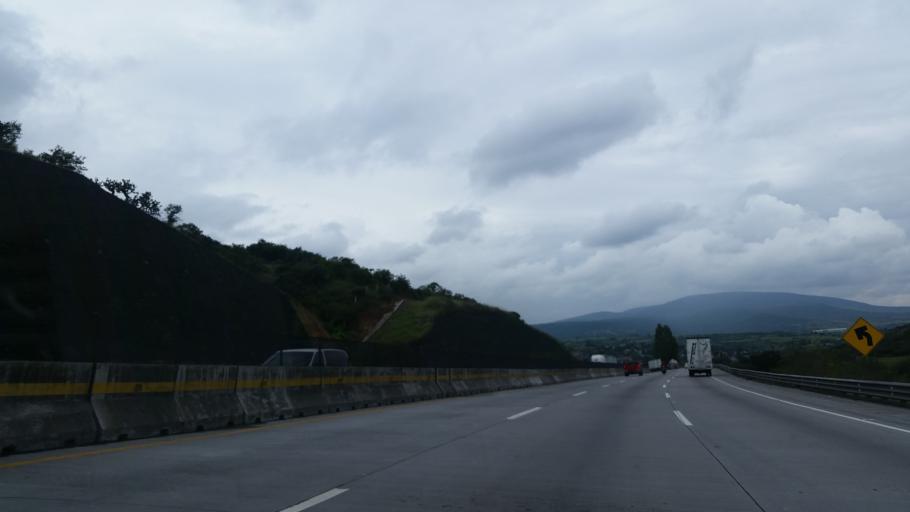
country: MX
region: Hidalgo
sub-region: Tepeji del Rio de Ocampo
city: Santiago Tlautla
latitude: 19.9311
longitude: -99.3814
